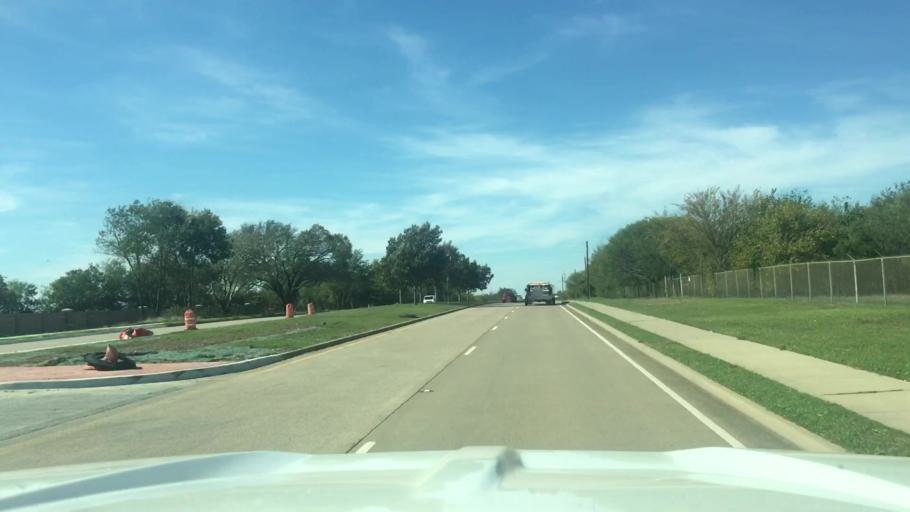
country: US
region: Texas
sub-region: Denton County
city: Denton
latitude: 33.2523
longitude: -97.1551
